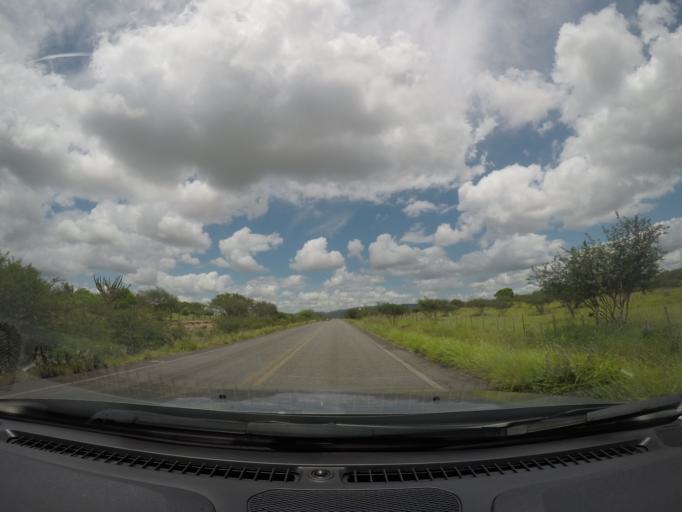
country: BR
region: Bahia
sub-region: Ipira
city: Ipira
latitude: -12.1938
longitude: -39.7692
